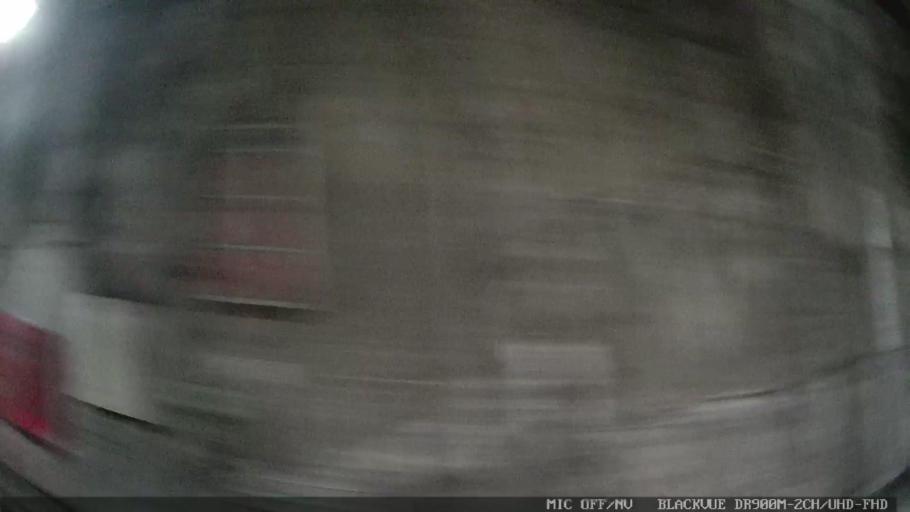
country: BR
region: Sao Paulo
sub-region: Cubatao
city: Cubatao
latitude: -23.8916
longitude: -46.4801
